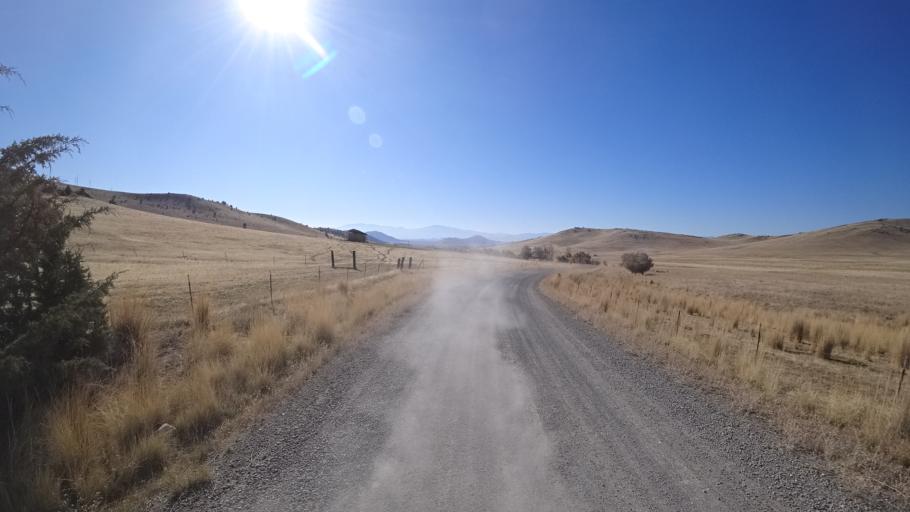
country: US
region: California
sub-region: Siskiyou County
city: Montague
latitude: 41.7461
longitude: -122.3635
